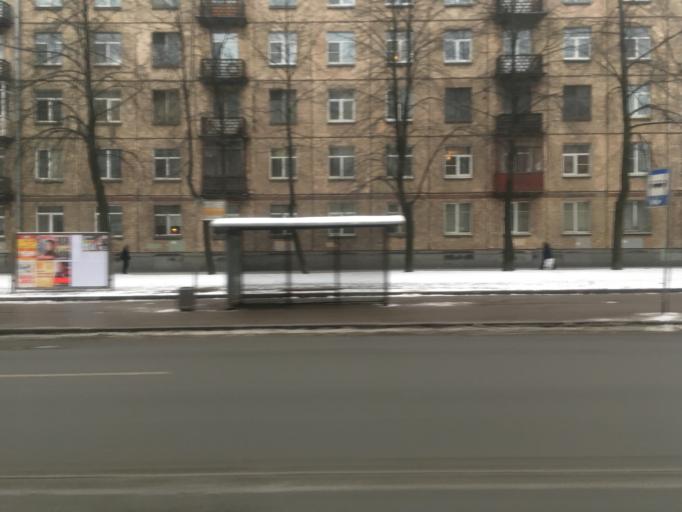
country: RU
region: St.-Petersburg
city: Obukhovo
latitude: 59.8727
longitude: 30.4379
